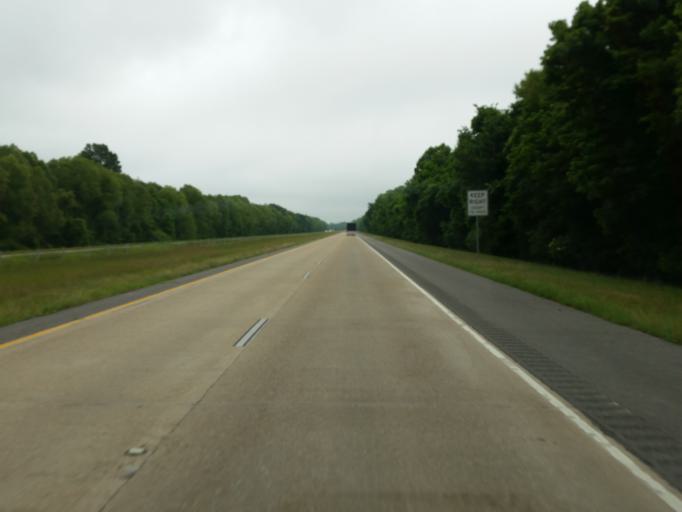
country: US
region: Louisiana
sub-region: Madison Parish
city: Tallulah
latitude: 32.3448
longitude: -91.0796
